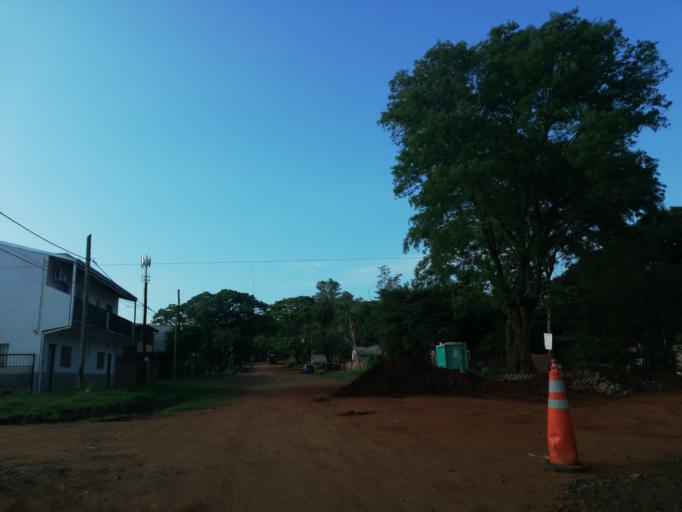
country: AR
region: Misiones
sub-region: Departamento de Capital
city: Posadas
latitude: -27.4000
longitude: -55.9248
